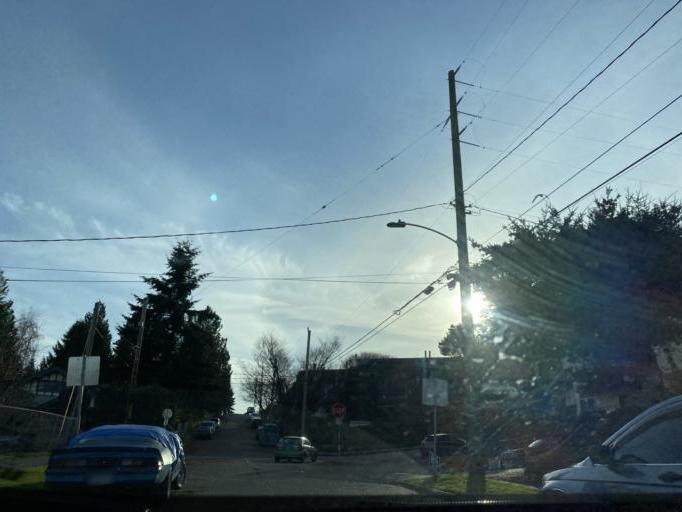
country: US
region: Washington
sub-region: King County
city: Seattle
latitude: 47.6544
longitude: -122.3874
